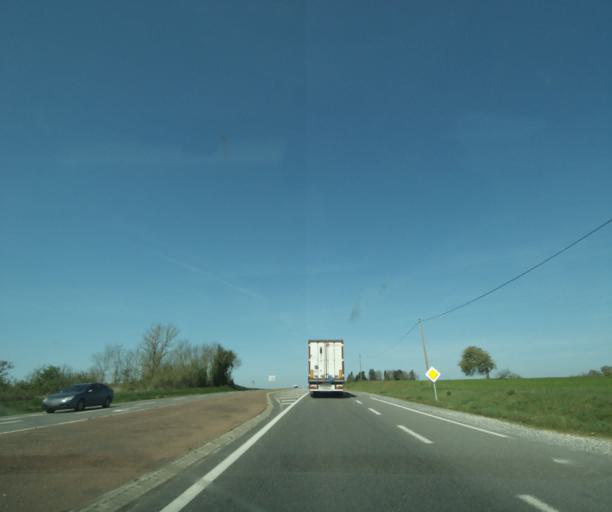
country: FR
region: Bourgogne
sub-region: Departement de la Nievre
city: Chantenay-Saint-Imbert
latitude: 46.7360
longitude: 3.1650
